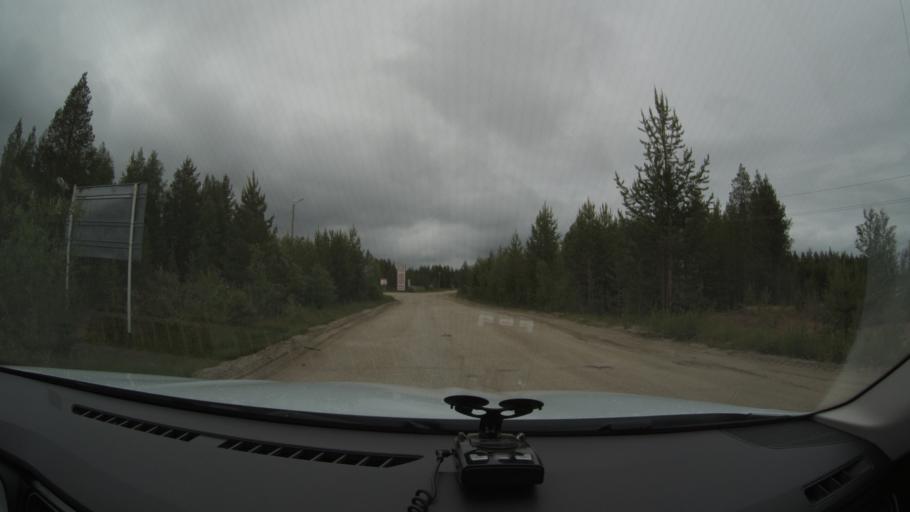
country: RU
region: Komi Republic
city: Kozhva
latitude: 65.1138
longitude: 57.0005
